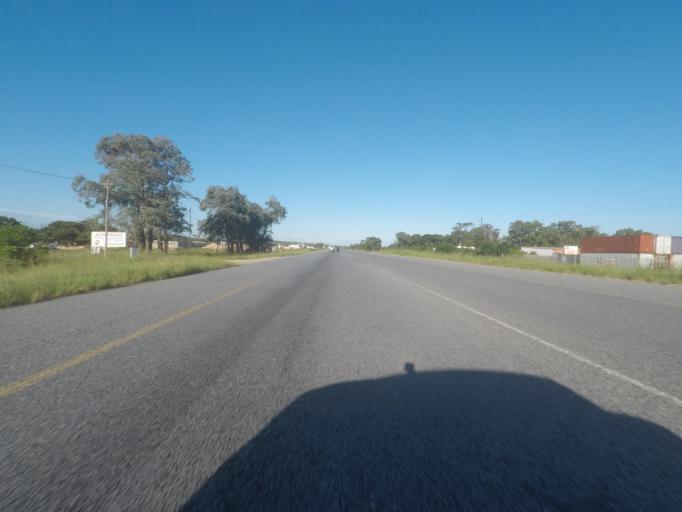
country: ZA
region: Eastern Cape
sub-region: Buffalo City Metropolitan Municipality
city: East London
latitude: -33.0563
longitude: 27.7996
